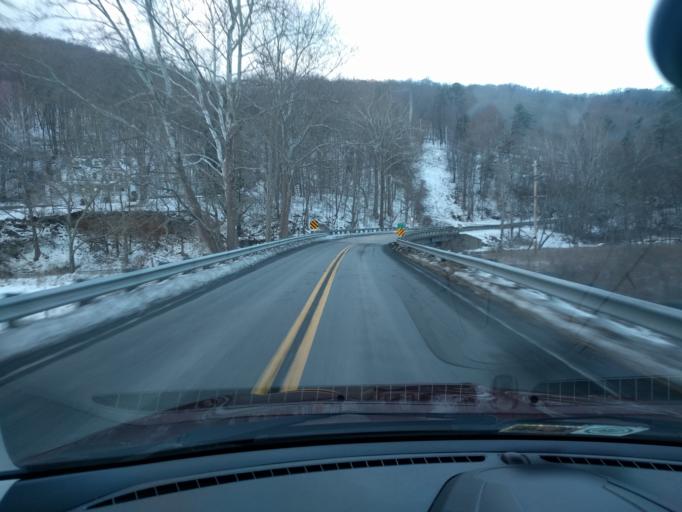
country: US
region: Virginia
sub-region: Bath County
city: Warm Springs
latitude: 38.0772
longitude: -79.8449
